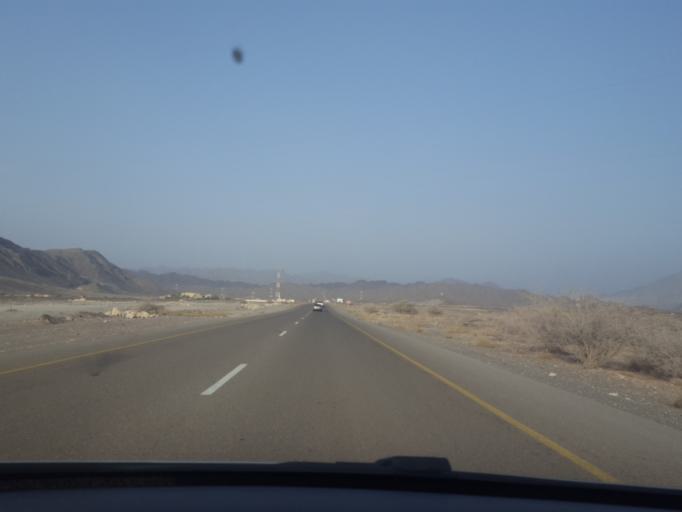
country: AE
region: Abu Dhabi
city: Al Ain
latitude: 24.0497
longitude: 56.0582
